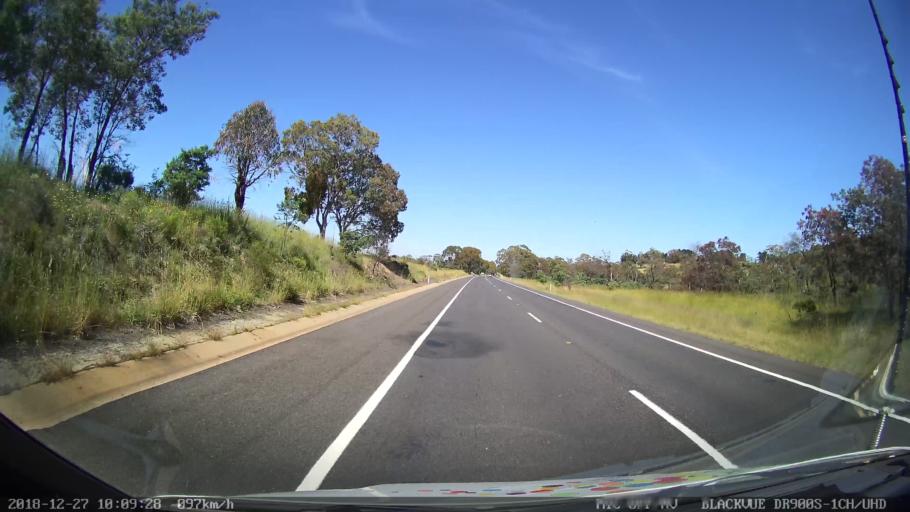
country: AU
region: New South Wales
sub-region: Lithgow
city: Portland
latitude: -33.4512
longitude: 149.8085
